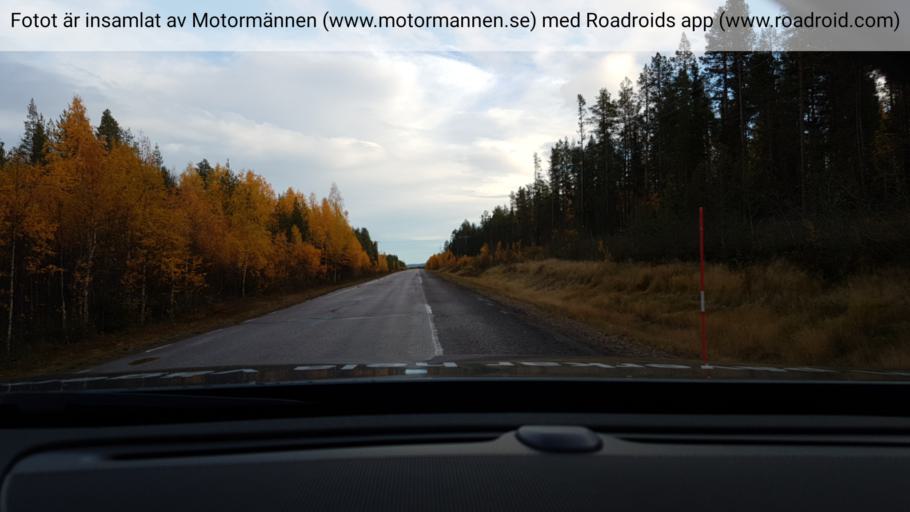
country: SE
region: Norrbotten
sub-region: Overkalix Kommun
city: OEverkalix
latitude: 67.0245
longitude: 22.5158
